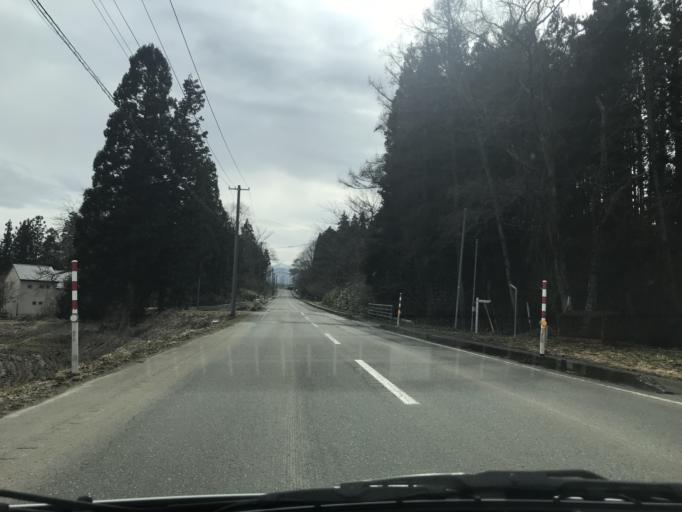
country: JP
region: Iwate
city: Hanamaki
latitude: 39.3401
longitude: 140.9778
